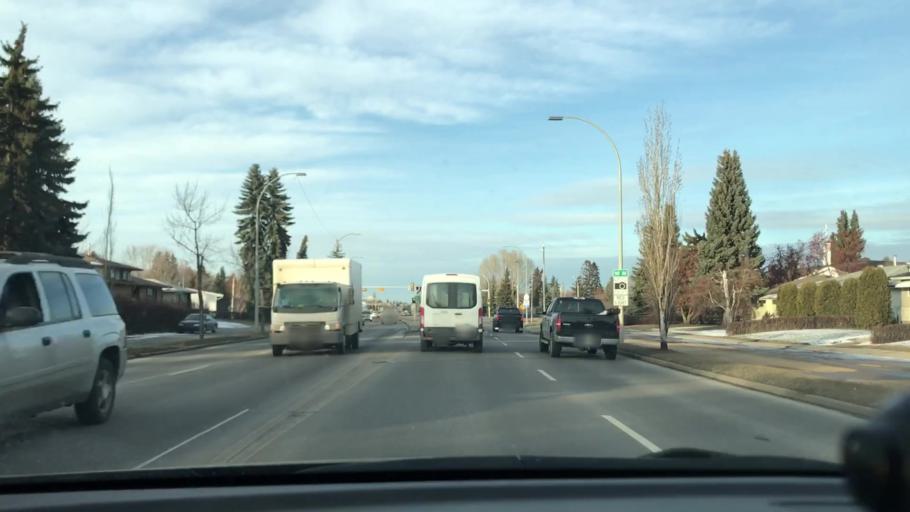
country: CA
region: Alberta
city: Edmonton
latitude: 53.5360
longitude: -113.4429
